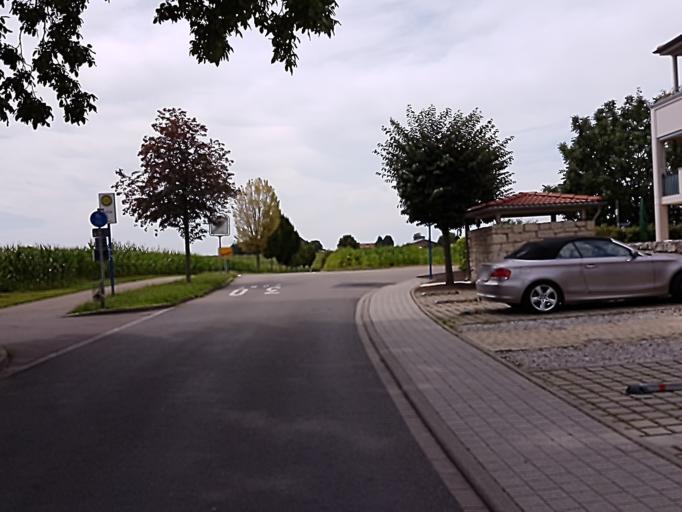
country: DE
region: Baden-Wuerttemberg
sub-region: Freiburg Region
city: Bad Krozingen
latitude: 47.9154
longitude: 7.6954
